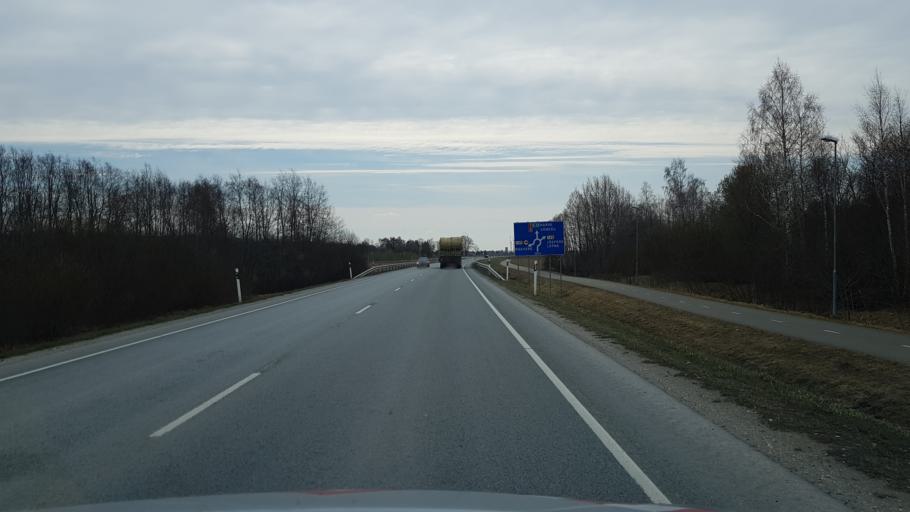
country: EE
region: Laeaene-Virumaa
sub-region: Rakvere linn
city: Rakvere
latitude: 59.3436
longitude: 26.3418
